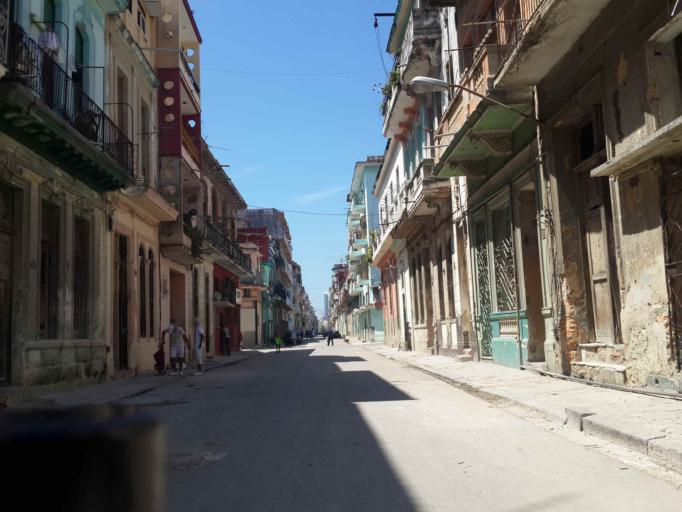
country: CU
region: La Habana
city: Centro Habana
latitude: 23.1408
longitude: -82.3645
